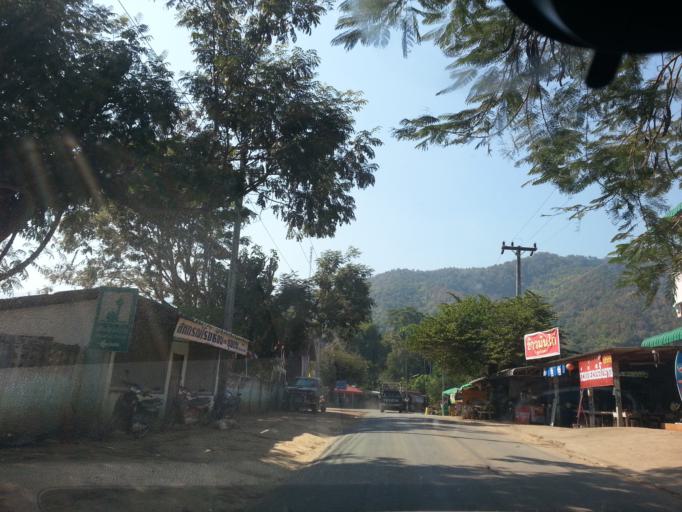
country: TH
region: Chiang Mai
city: Chai Prakan
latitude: 19.8155
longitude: 99.1046
